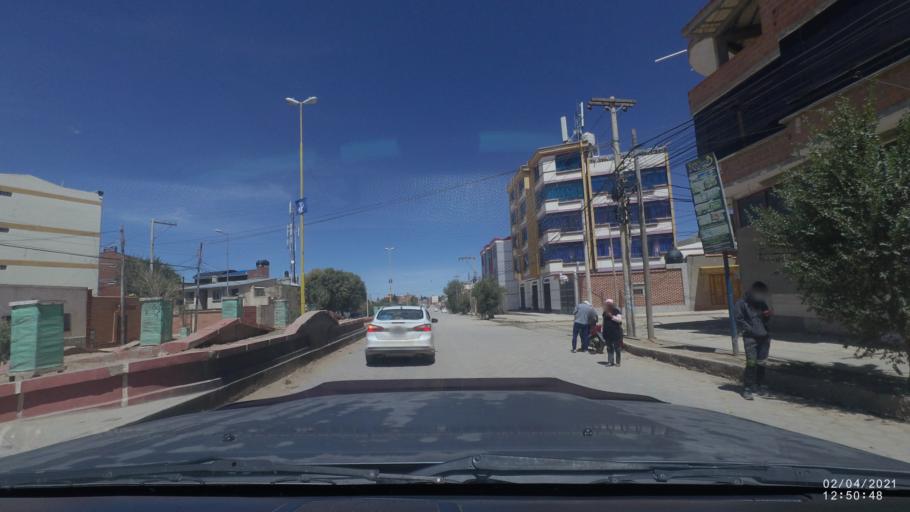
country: BO
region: Oruro
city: Oruro
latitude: -17.9779
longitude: -67.1375
